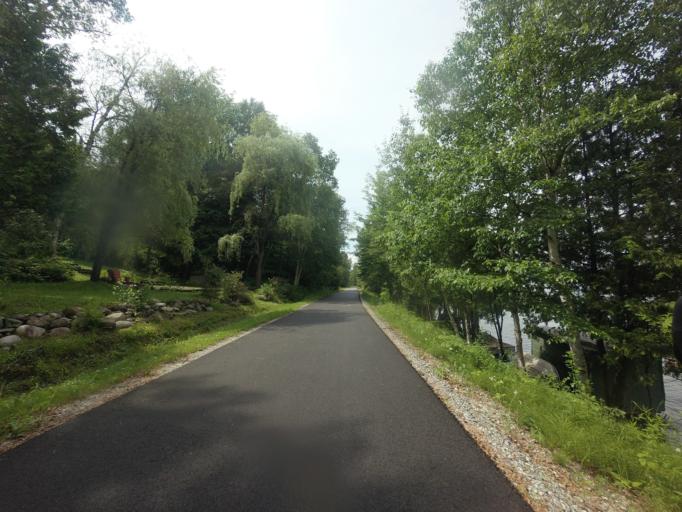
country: CA
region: Quebec
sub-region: Outaouais
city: Maniwaki
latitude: 46.2015
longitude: -76.0465
